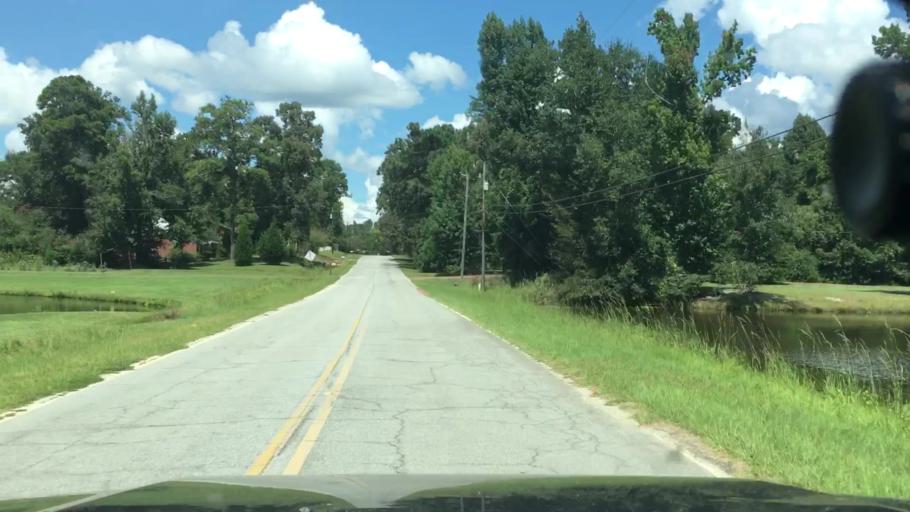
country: US
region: Georgia
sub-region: Bibb County
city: West Point
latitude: 32.8030
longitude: -83.7935
